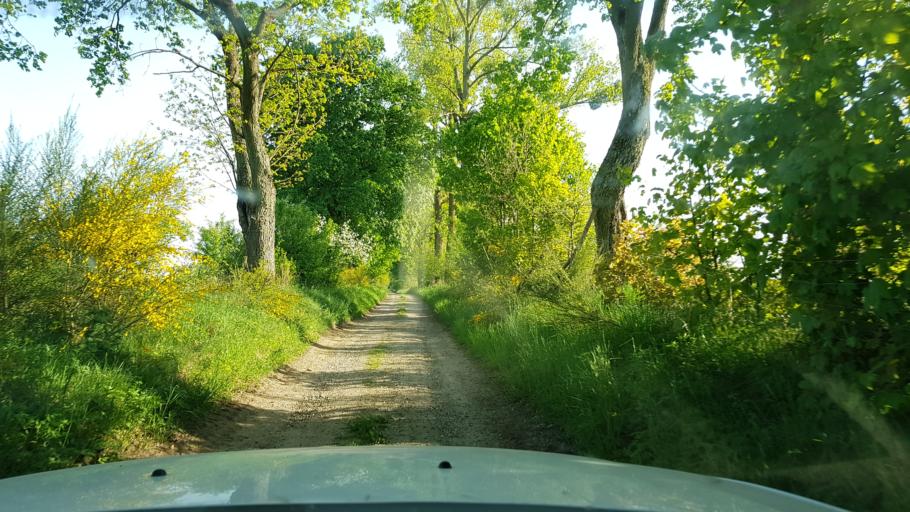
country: PL
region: West Pomeranian Voivodeship
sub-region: Powiat lobeski
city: Resko
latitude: 53.6964
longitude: 15.3360
